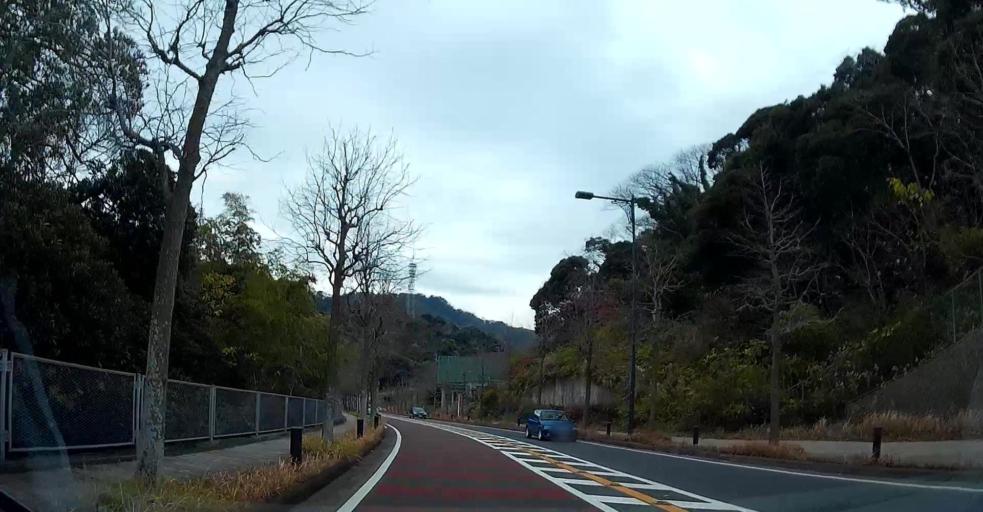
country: JP
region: Kanagawa
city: Yokosuka
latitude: 35.2247
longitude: 139.6654
